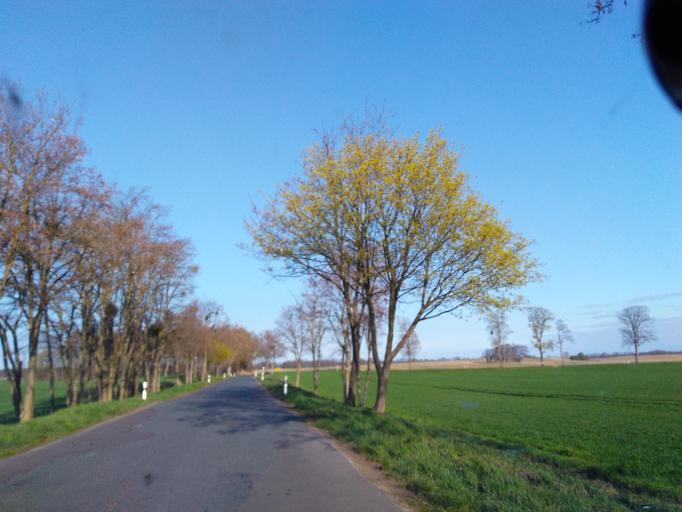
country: DE
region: Brandenburg
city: Protzel
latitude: 52.6598
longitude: 14.0455
